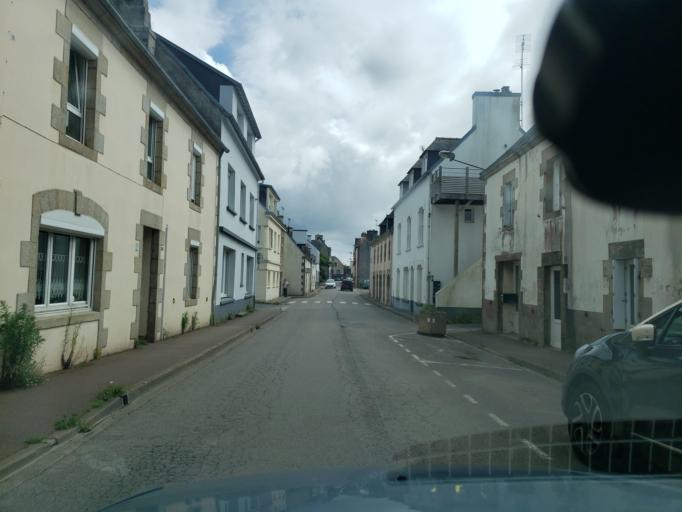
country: FR
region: Brittany
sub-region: Departement du Finistere
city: Ploneour-Lanvern
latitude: 47.9049
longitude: -4.2824
